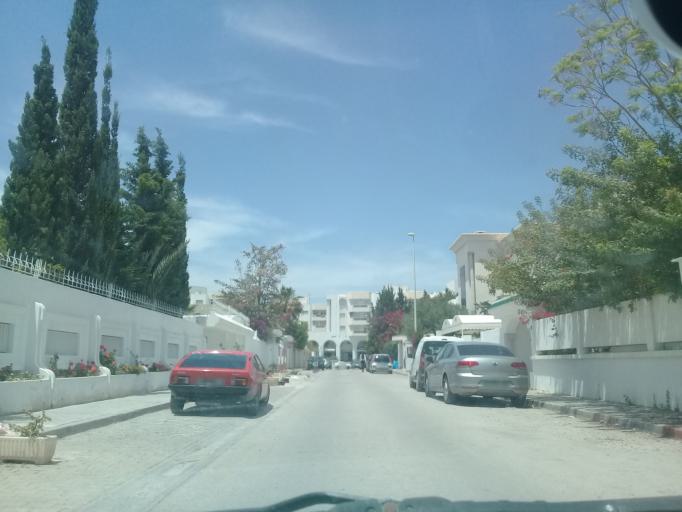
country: TN
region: Ariana
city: Ariana
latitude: 36.8347
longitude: 10.2328
